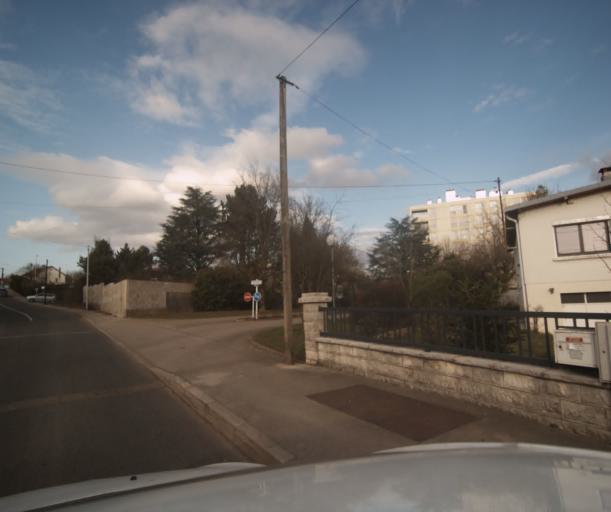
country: FR
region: Franche-Comte
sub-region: Departement du Doubs
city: Besancon
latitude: 47.2581
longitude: 6.0287
